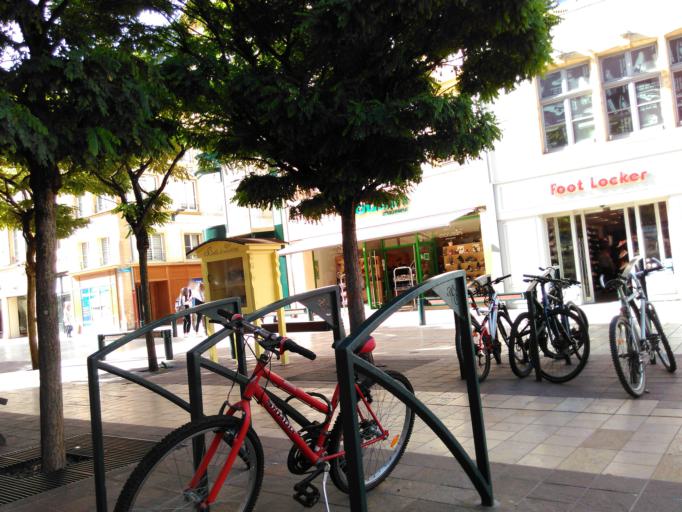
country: FR
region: Lorraine
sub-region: Departement de la Moselle
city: Thionville
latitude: 49.3579
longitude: 6.1673
